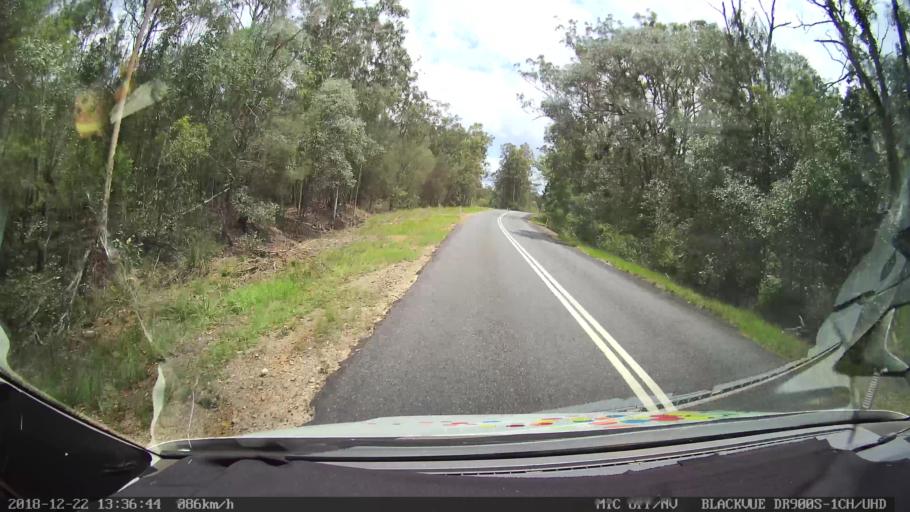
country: AU
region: New South Wales
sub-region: Clarence Valley
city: Coutts Crossing
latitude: -29.8827
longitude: 152.7925
